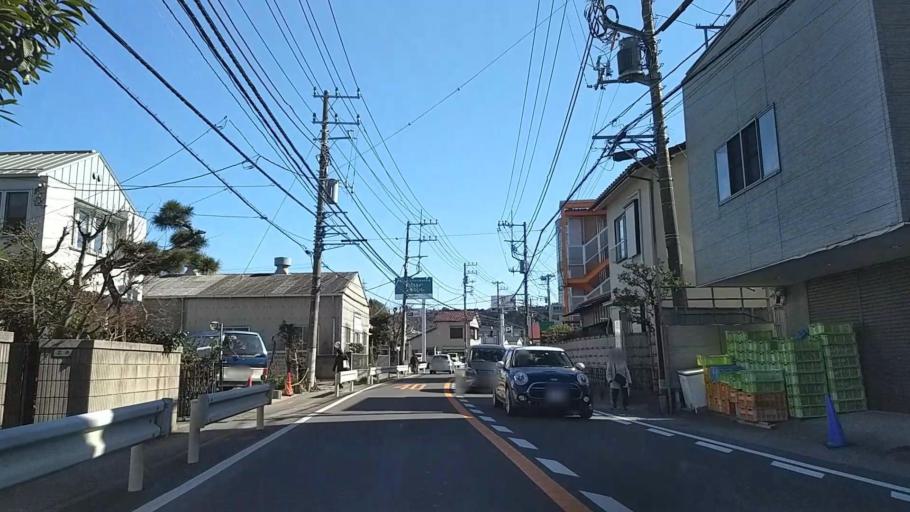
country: JP
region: Kanagawa
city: Kamakura
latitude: 35.3299
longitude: 139.5199
